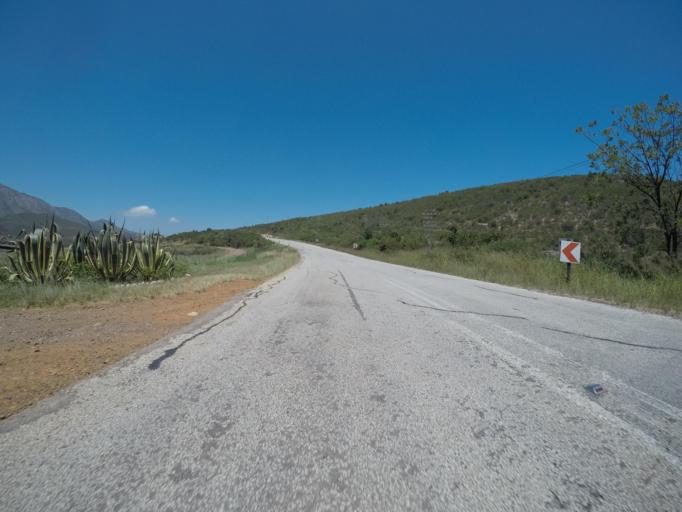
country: ZA
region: Eastern Cape
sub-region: Cacadu District Municipality
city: Kareedouw
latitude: -33.9096
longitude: 24.1601
